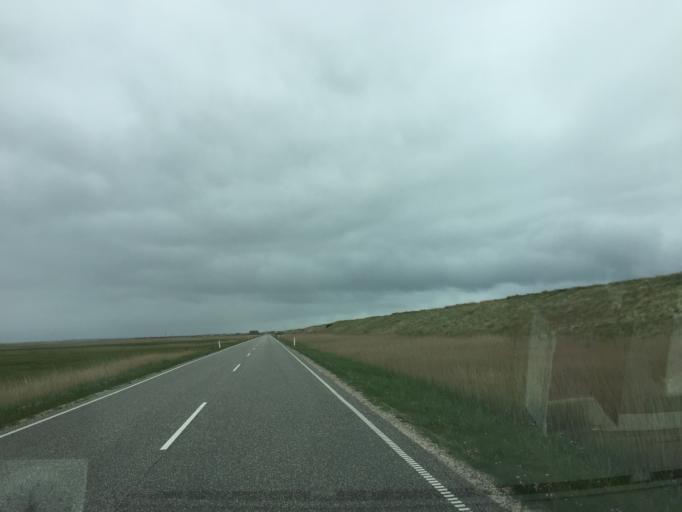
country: DK
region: Central Jutland
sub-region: Lemvig Kommune
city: Harboore
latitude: 56.4034
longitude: 8.1220
